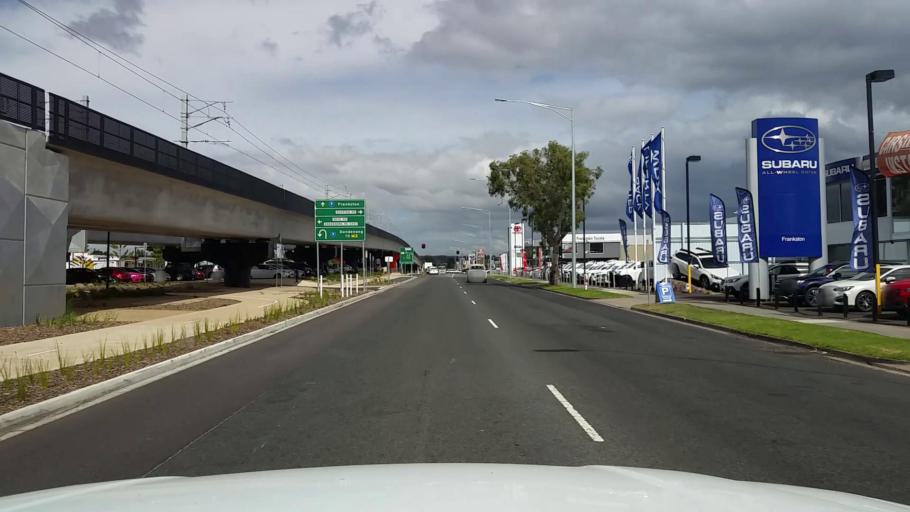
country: AU
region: Victoria
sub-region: Frankston
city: Frankston East
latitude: -38.1284
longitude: 145.1322
